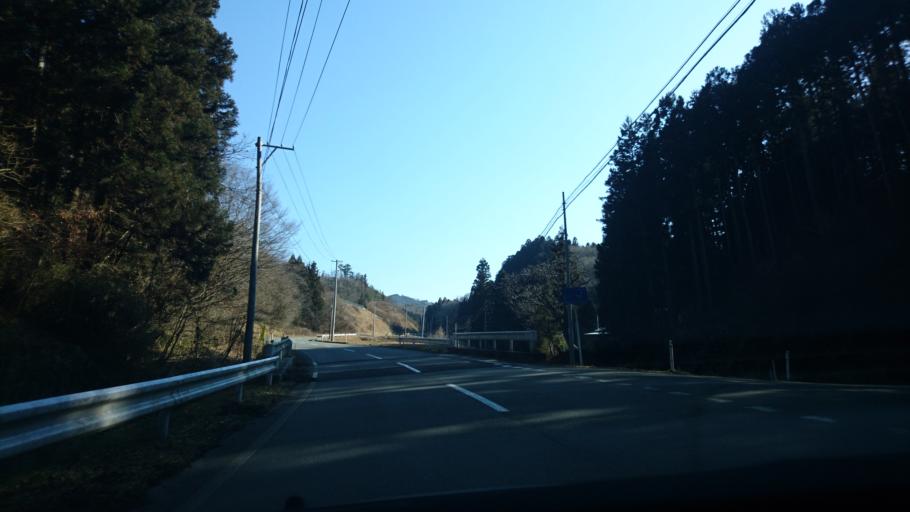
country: JP
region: Iwate
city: Ichinoseki
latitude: 38.8423
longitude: 141.2976
